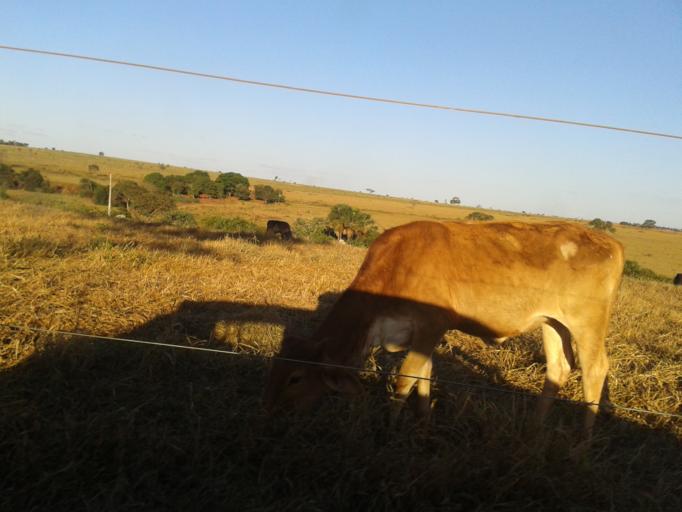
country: BR
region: Minas Gerais
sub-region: Centralina
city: Centralina
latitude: -18.7622
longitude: -49.2008
